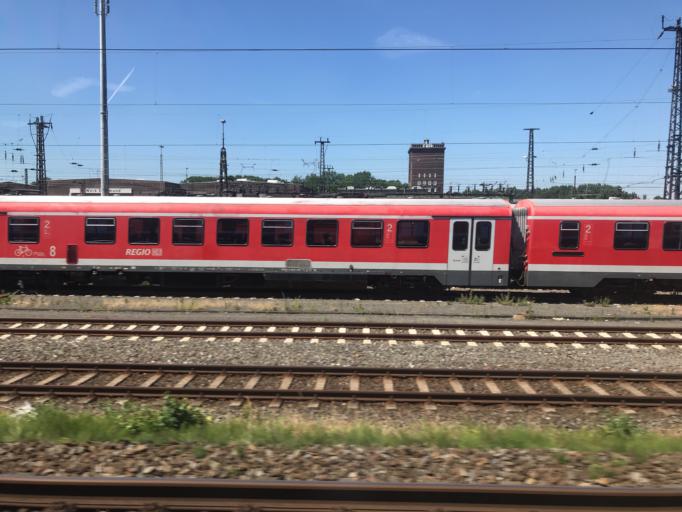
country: DE
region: North Rhine-Westphalia
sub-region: Regierungsbezirk Arnsberg
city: Dortmund
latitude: 51.5234
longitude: 7.4972
